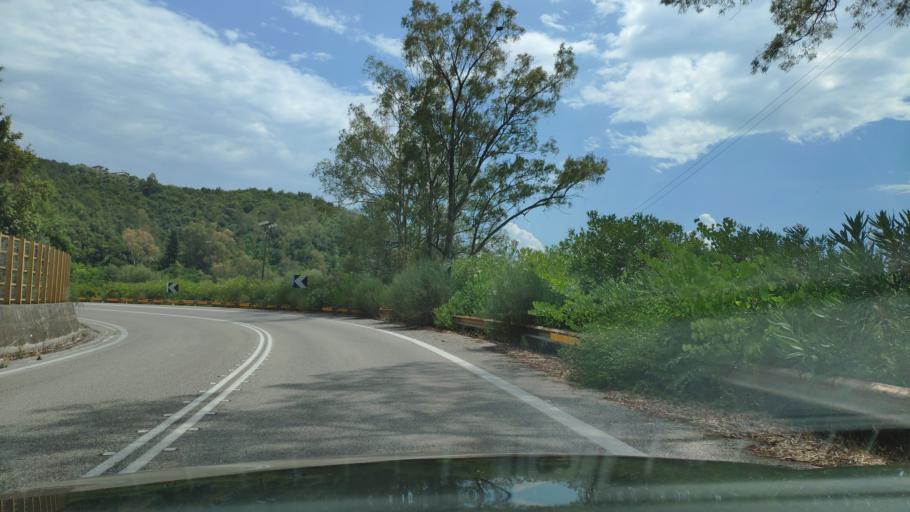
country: GR
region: West Greece
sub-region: Nomos Aitolias kai Akarnanias
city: Menidi
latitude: 39.0337
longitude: 21.1262
